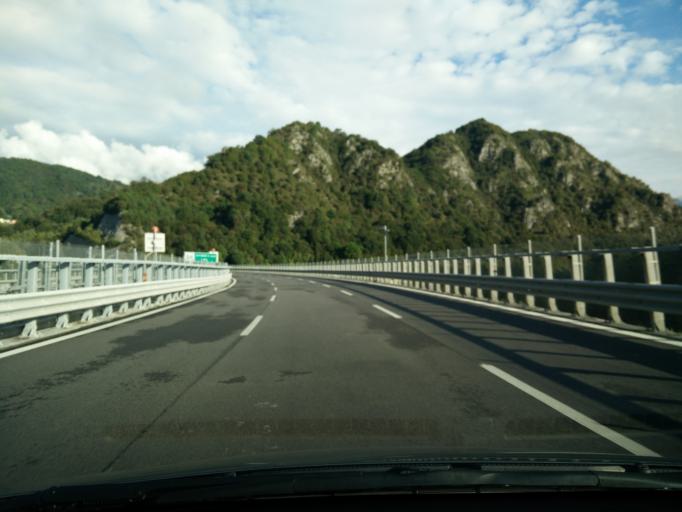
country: IT
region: Veneto
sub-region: Provincia di Treviso
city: Vittorio Veneto
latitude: 45.9771
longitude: 12.2827
